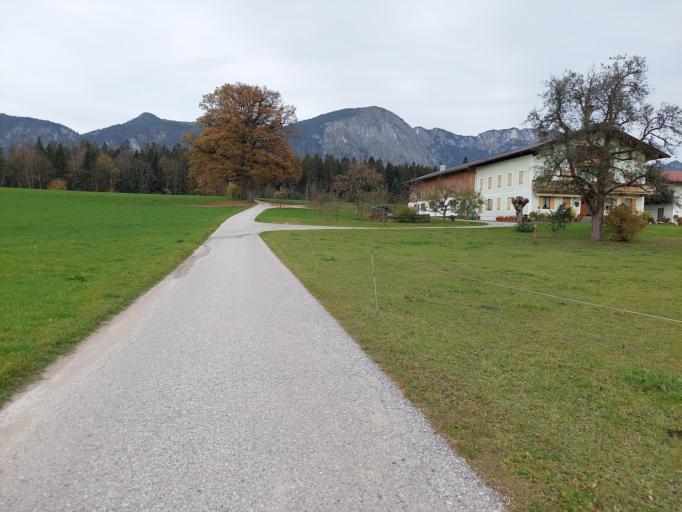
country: AT
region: Tyrol
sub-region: Politischer Bezirk Kufstein
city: Angath
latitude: 47.5014
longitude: 12.0433
